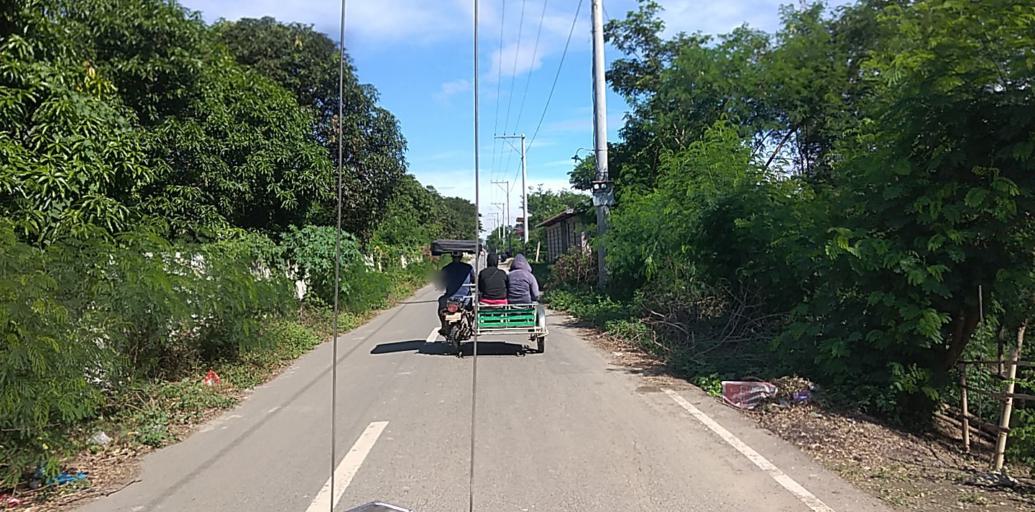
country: PH
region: Central Luzon
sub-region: Province of Pampanga
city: Candaba
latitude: 15.0743
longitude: 120.8071
